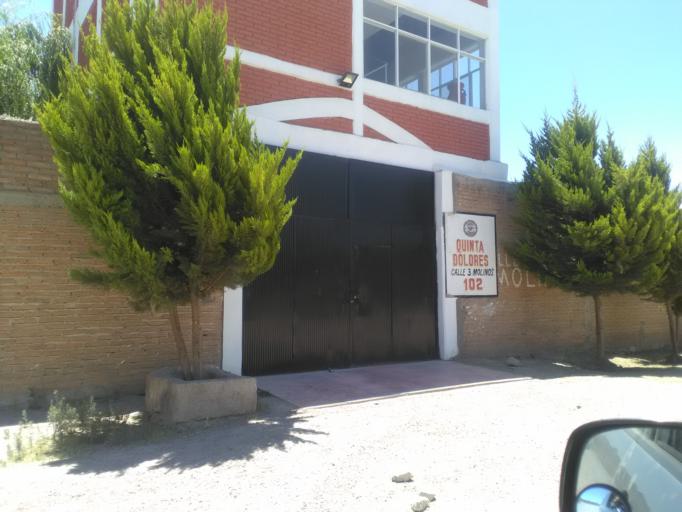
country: MX
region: Durango
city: Victoria de Durango
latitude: 23.9852
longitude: -104.6668
